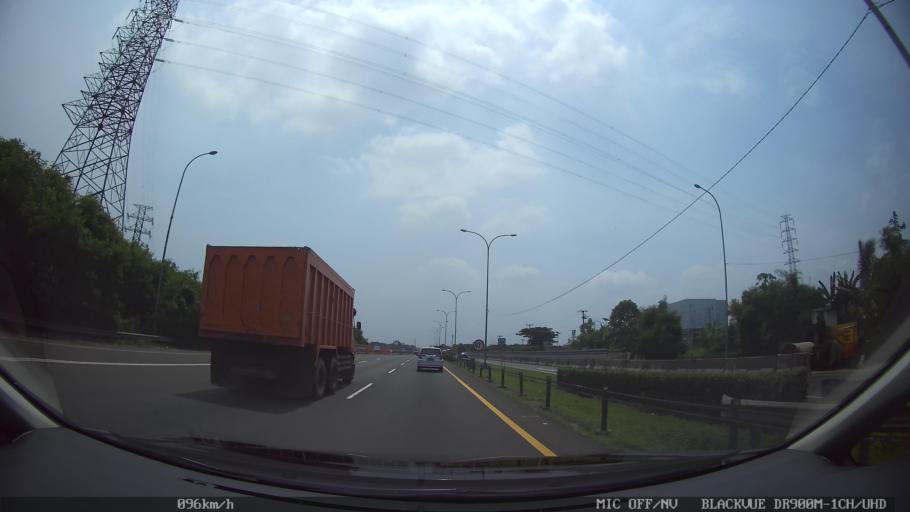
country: ID
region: West Java
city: Kresek
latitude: -6.1713
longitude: 106.3448
